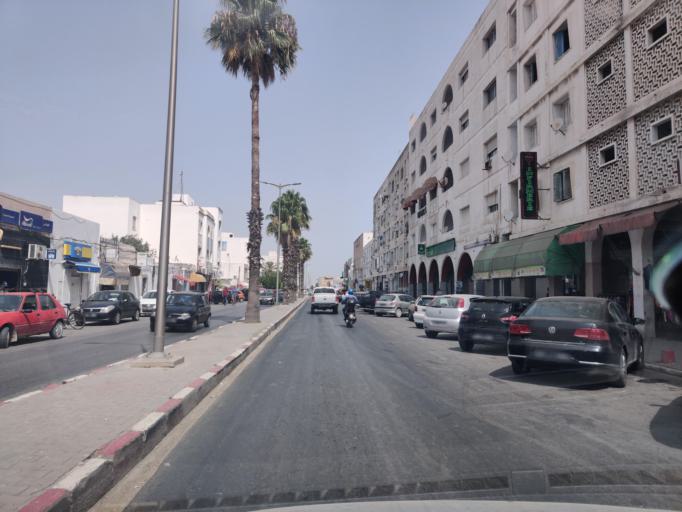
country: TN
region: Nabul
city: Bu `Urqub
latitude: 36.5993
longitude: 10.4984
